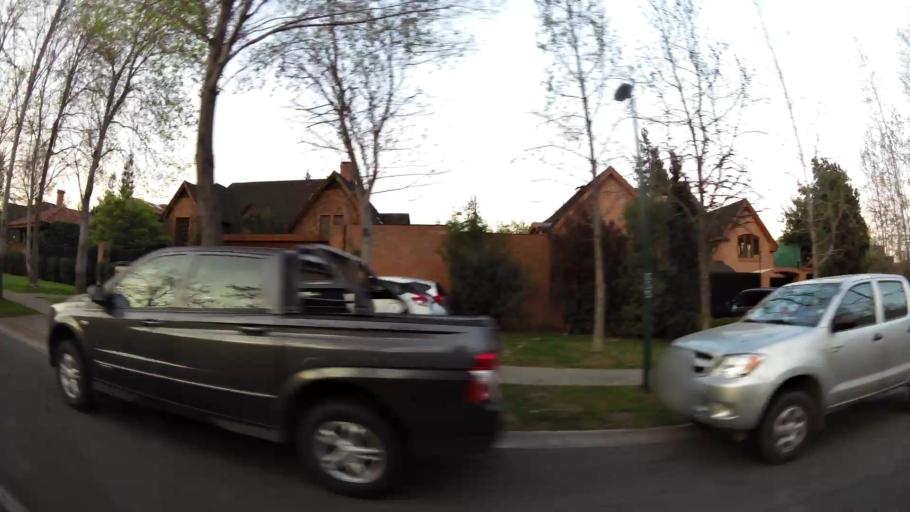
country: CL
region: Santiago Metropolitan
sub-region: Provincia de Chacabuco
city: Chicureo Abajo
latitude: -33.3423
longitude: -70.5532
